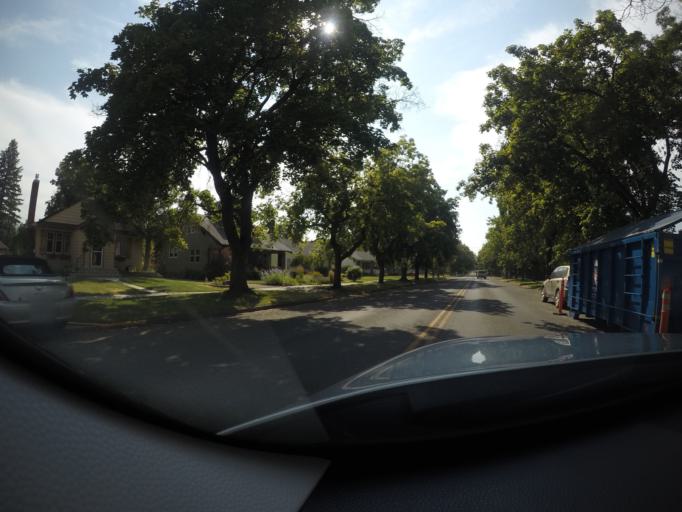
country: US
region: Montana
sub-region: Missoula County
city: Missoula
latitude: 46.8571
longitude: -113.9915
